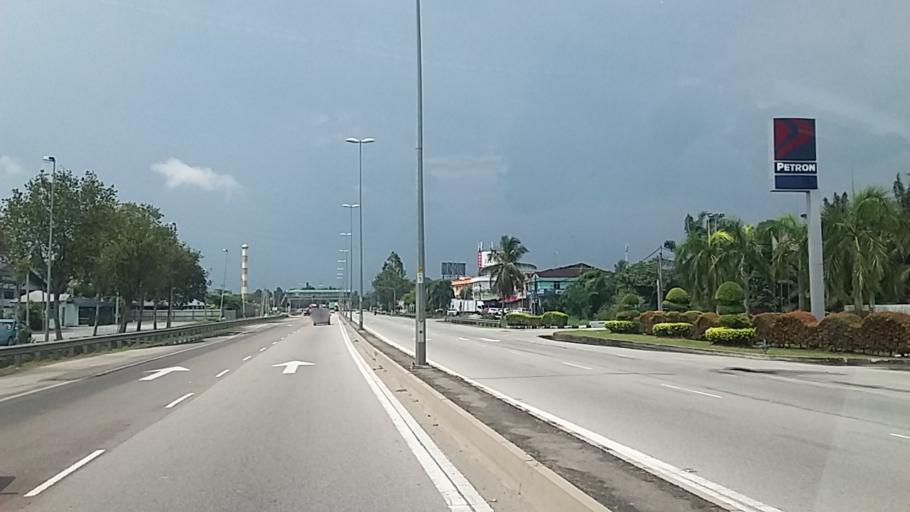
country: MY
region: Johor
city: Parit Raja
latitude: 1.8560
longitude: 103.0964
